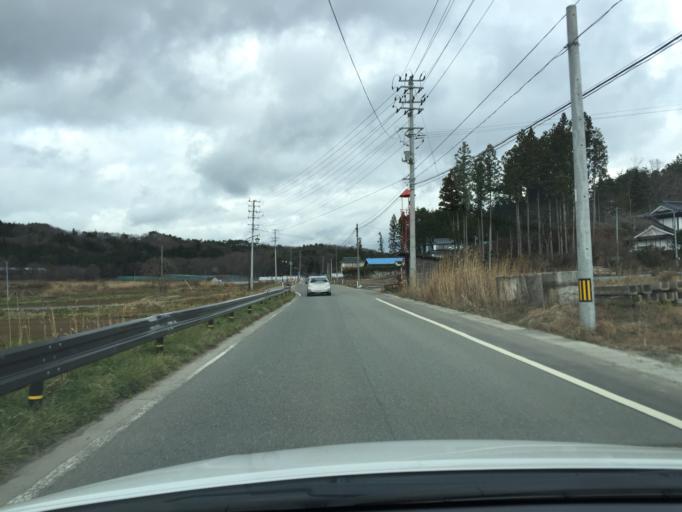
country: JP
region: Fukushima
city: Yanagawamachi-saiwaicho
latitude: 37.7044
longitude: 140.6961
